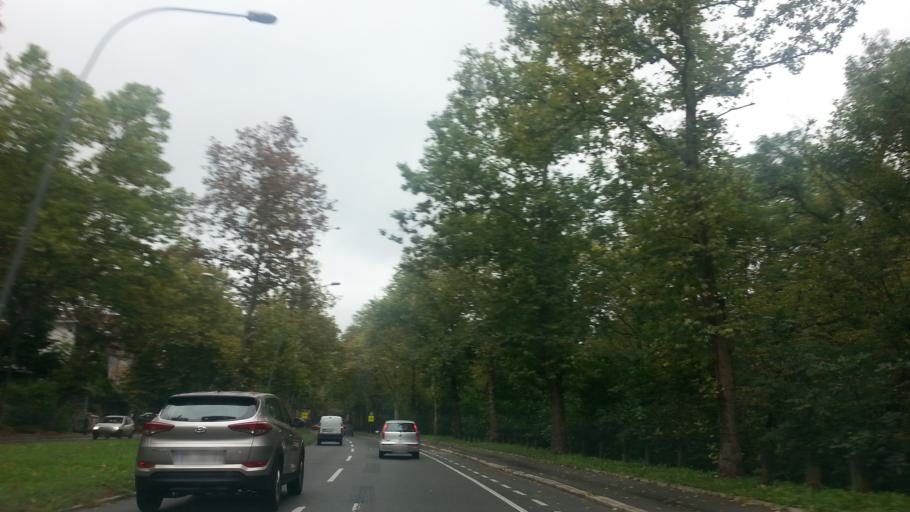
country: RS
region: Central Serbia
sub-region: Belgrade
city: Vozdovac
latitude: 44.7785
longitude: 20.4696
